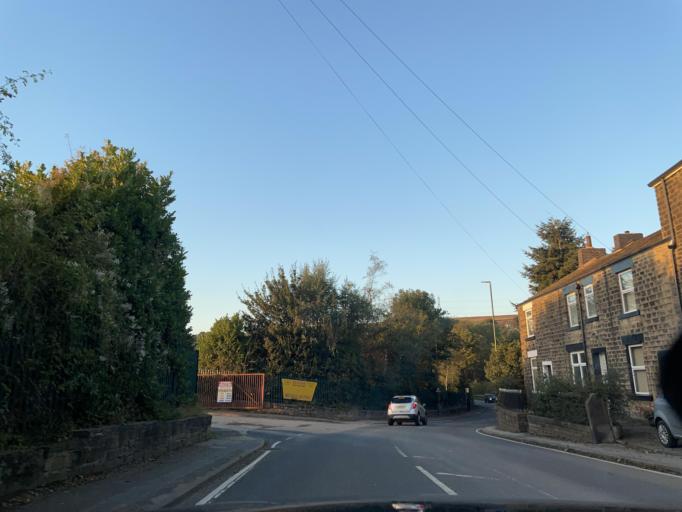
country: GB
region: England
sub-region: Borough of Tameside
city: Longdendale
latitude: 53.4675
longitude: -1.9707
